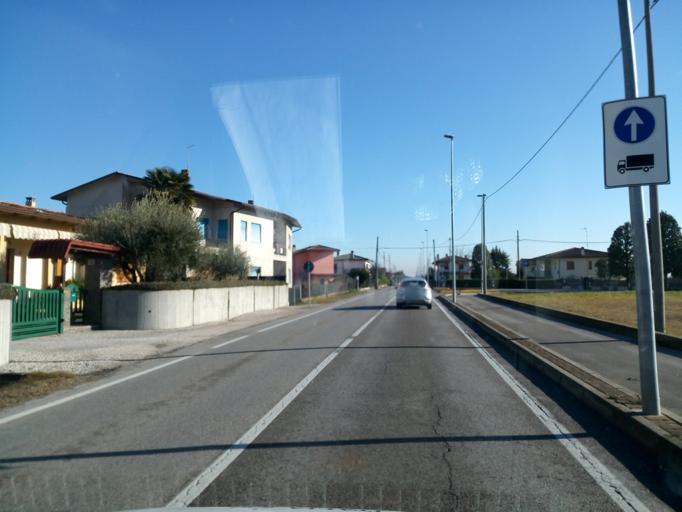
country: IT
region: Veneto
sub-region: Provincia di Treviso
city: Priula-Colfosco
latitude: 45.8200
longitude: 12.2638
